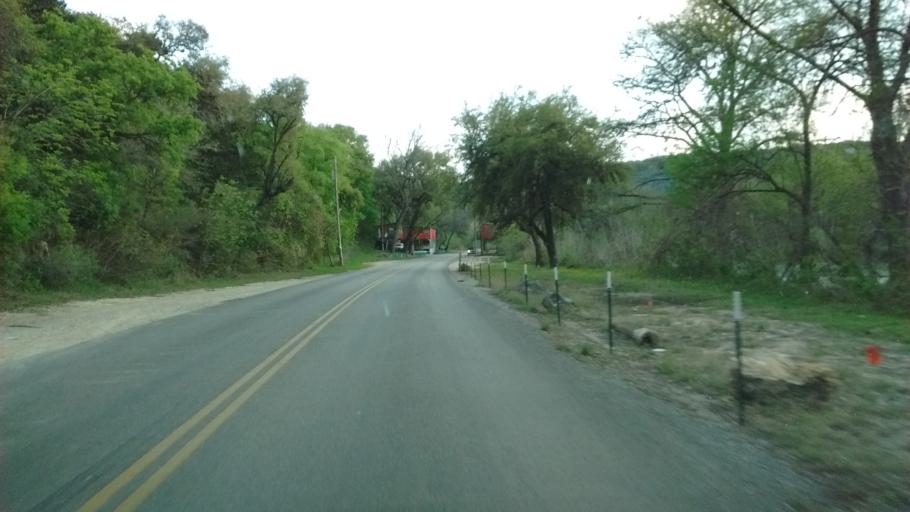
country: US
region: Texas
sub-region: Comal County
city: New Braunfels
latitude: 29.7719
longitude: -98.1583
